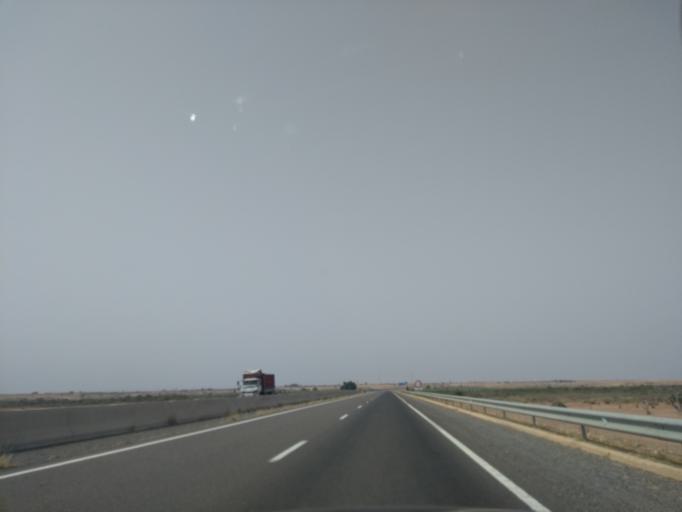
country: MA
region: Marrakech-Tensift-Al Haouz
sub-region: Marrakech
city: Marrakesh
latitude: 31.7353
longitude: -8.2161
